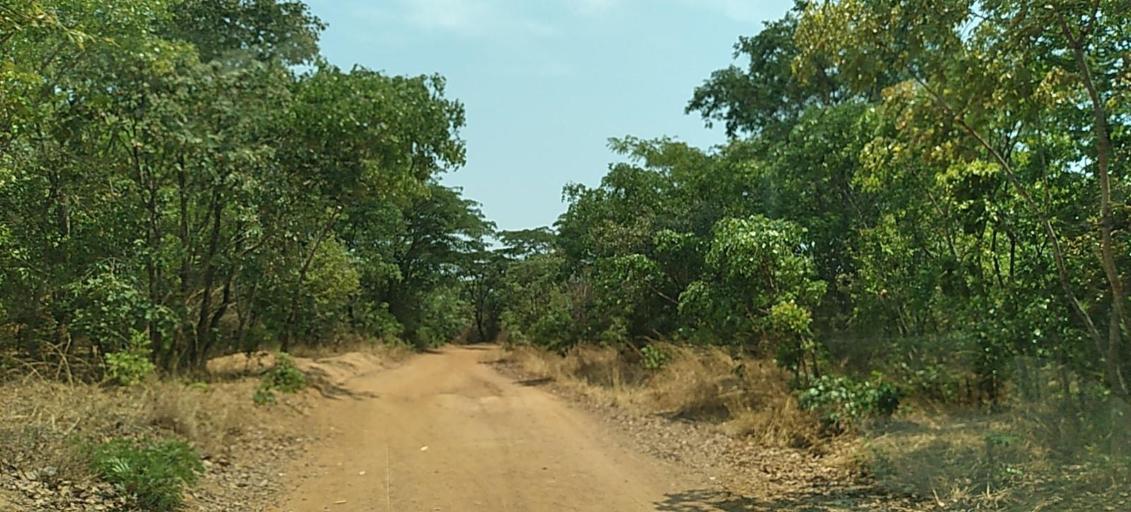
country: ZM
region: Copperbelt
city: Ndola
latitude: -13.0495
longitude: 28.7373
